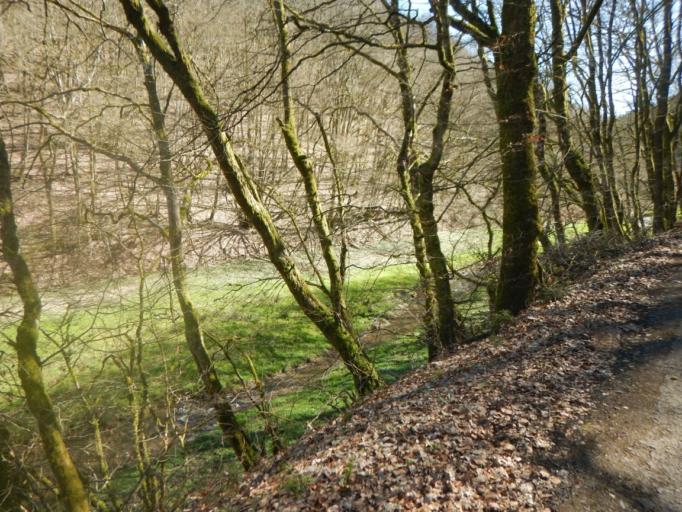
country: LU
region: Diekirch
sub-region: Canton de Wiltz
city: Eschweiler
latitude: 49.9736
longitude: 5.9597
